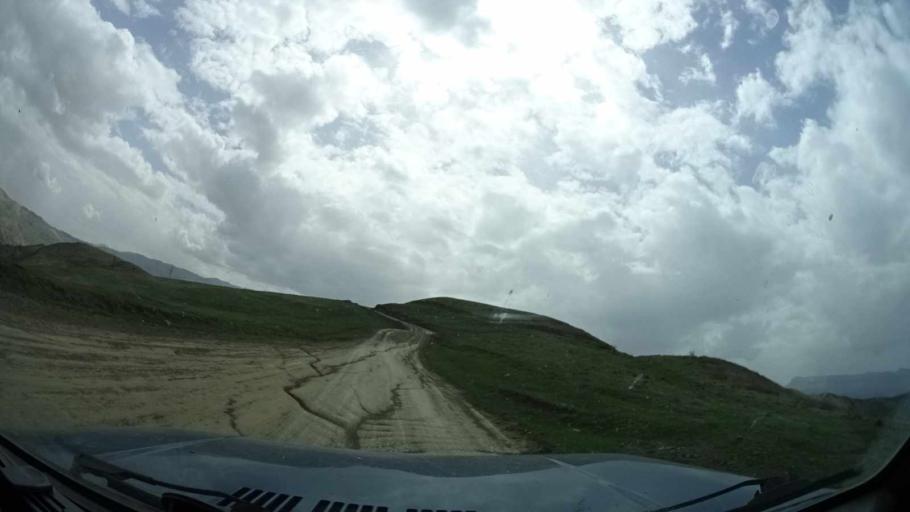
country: RU
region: Dagestan
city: Kubachi
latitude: 42.0866
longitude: 47.5665
